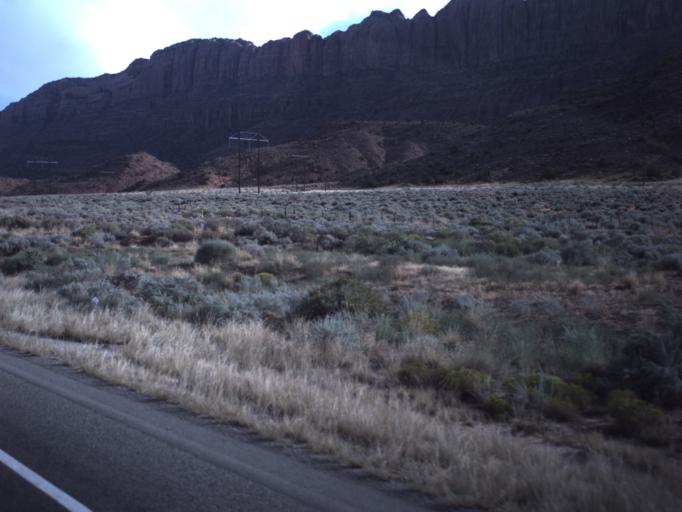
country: US
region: Utah
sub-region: Grand County
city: Moab
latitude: 38.5086
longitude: -109.4839
